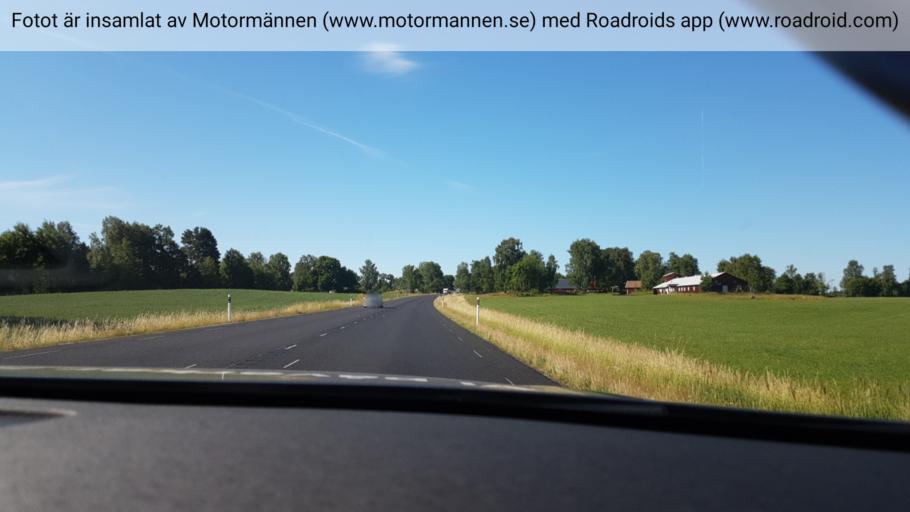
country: SE
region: Vaestra Goetaland
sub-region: Falkopings Kommun
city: Falkoeping
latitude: 57.9685
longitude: 13.5293
